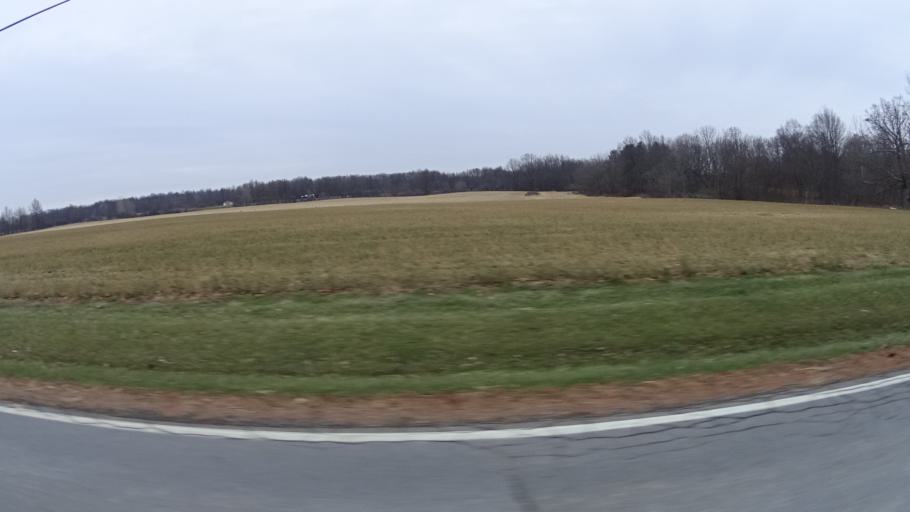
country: US
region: Ohio
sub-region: Lorain County
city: Grafton
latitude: 41.2425
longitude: -82.0425
